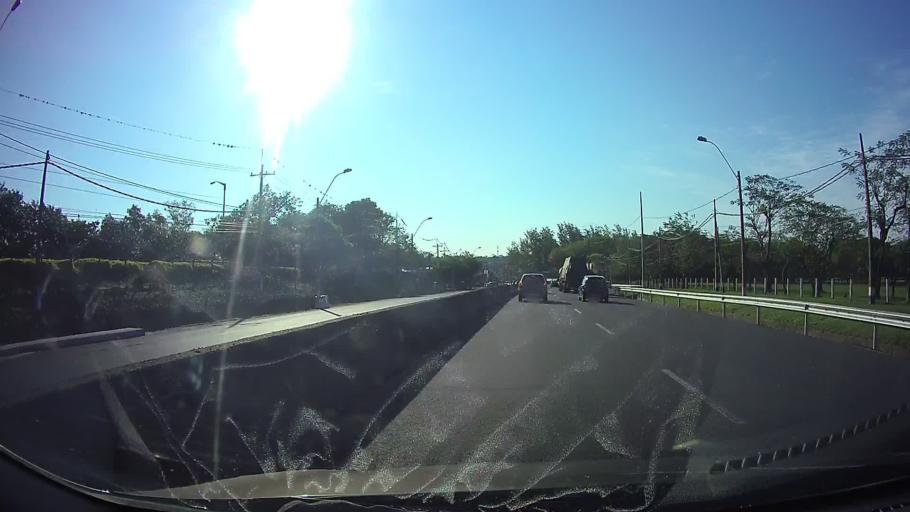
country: PY
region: Central
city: Capiata
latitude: -25.3615
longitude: -57.4301
